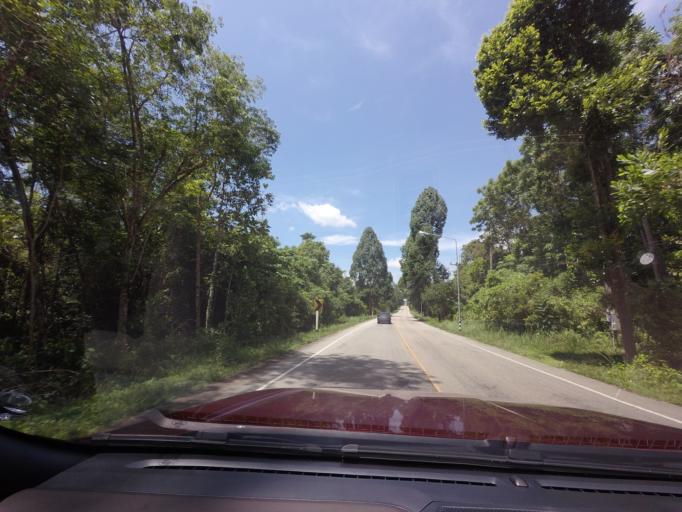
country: TH
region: Narathiwat
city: Chanae
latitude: 6.1855
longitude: 101.6949
